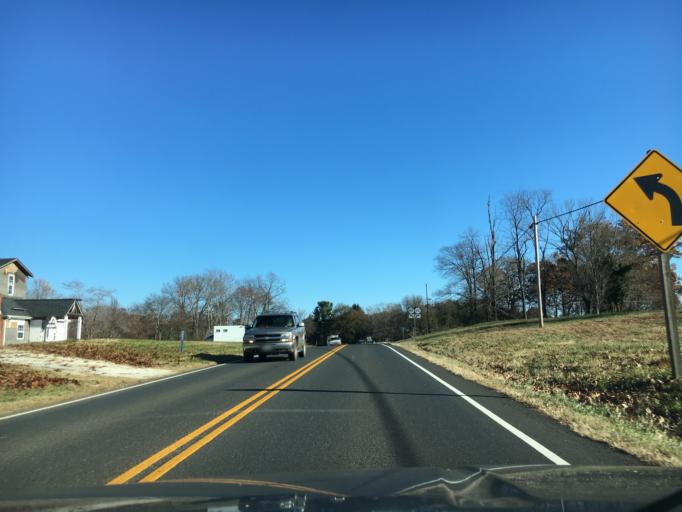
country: US
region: Virginia
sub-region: Appomattox County
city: Appomattox
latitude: 37.4095
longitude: -78.7657
